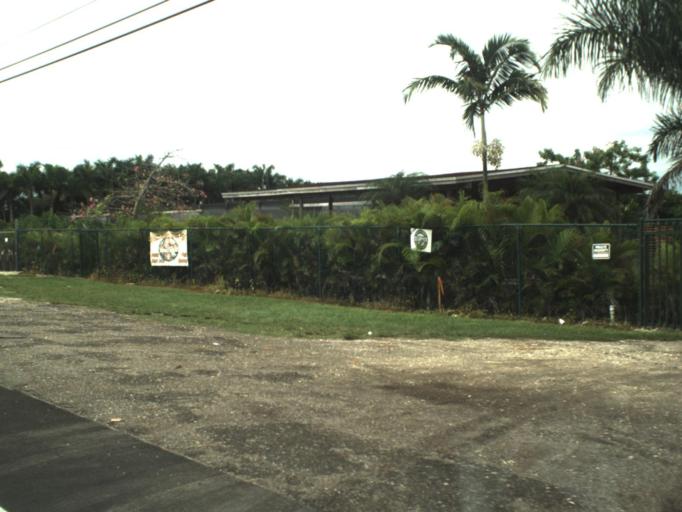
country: US
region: Florida
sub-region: Miami-Dade County
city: Richmond West
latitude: 25.5736
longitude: -80.4783
